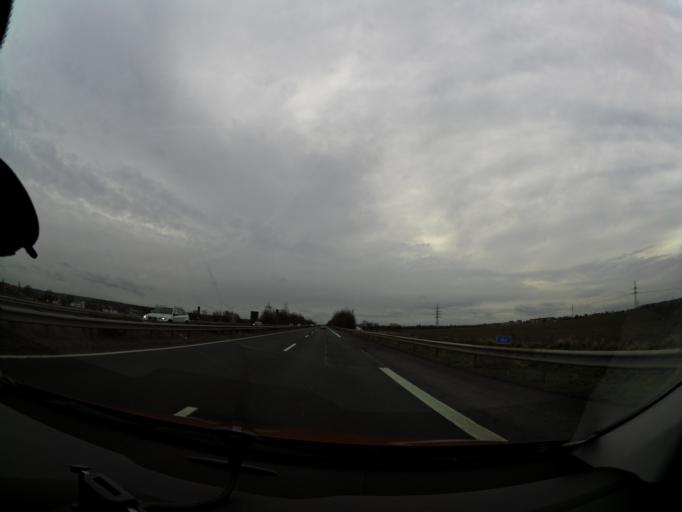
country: DE
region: Lower Saxony
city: Leiferde
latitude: 52.1726
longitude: 10.5020
